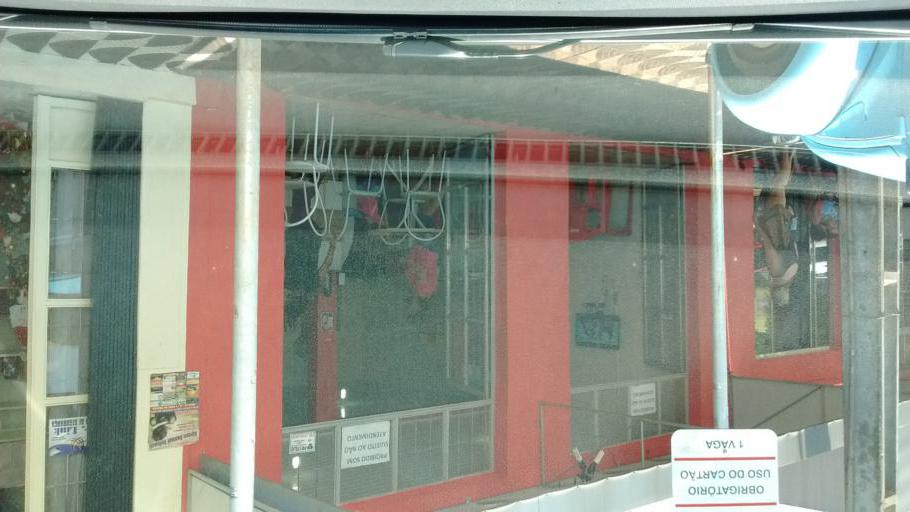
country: BR
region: Parana
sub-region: Corbelia
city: Corbelia
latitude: -24.5411
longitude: -52.9901
